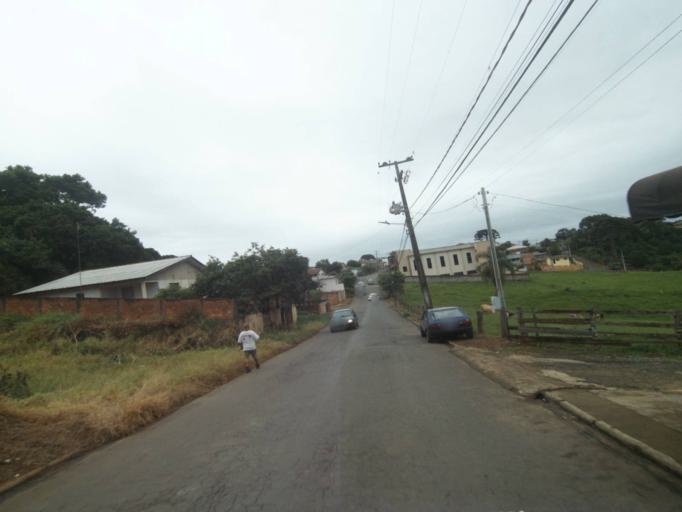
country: BR
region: Parana
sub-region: Telemaco Borba
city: Telemaco Borba
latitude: -24.3232
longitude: -50.6555
